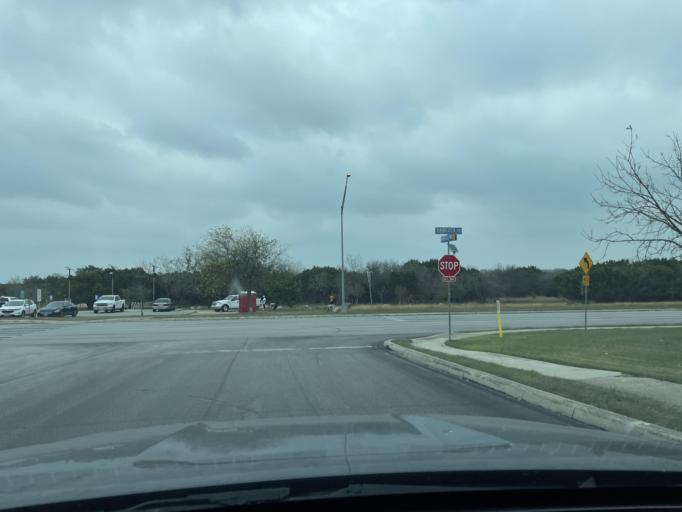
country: US
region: Texas
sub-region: Bexar County
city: Helotes
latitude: 29.5596
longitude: -98.6310
